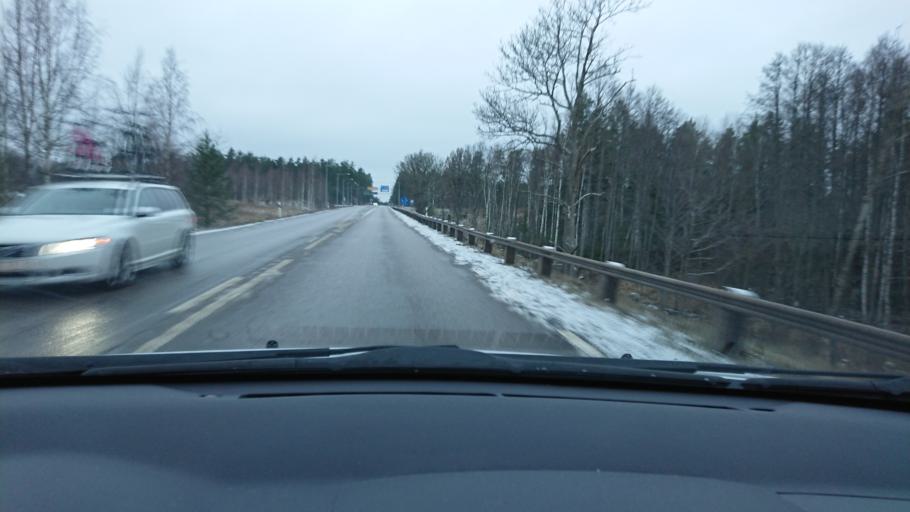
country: SE
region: Kalmar
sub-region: Hultsfreds Kommun
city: Hultsfred
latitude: 57.4866
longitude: 15.8285
